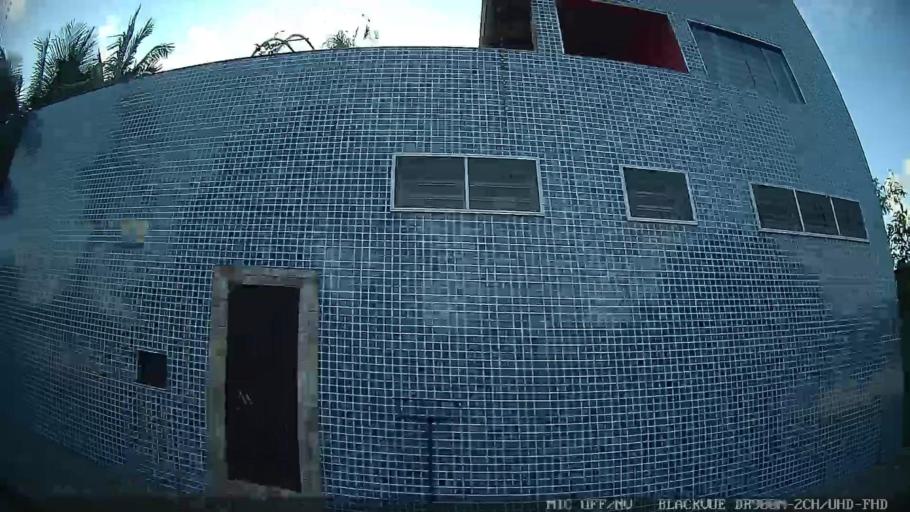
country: BR
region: Sao Paulo
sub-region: Itanhaem
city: Itanhaem
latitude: -24.1785
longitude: -46.8268
